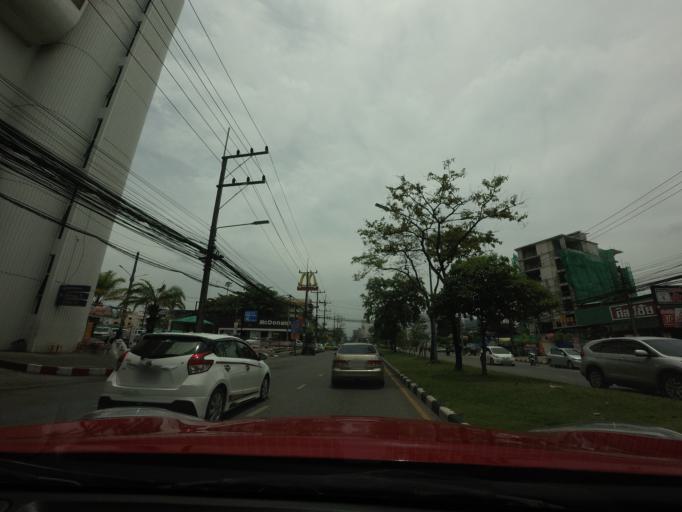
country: TH
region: Songkhla
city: Hat Yai
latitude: 6.9982
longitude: 100.4780
